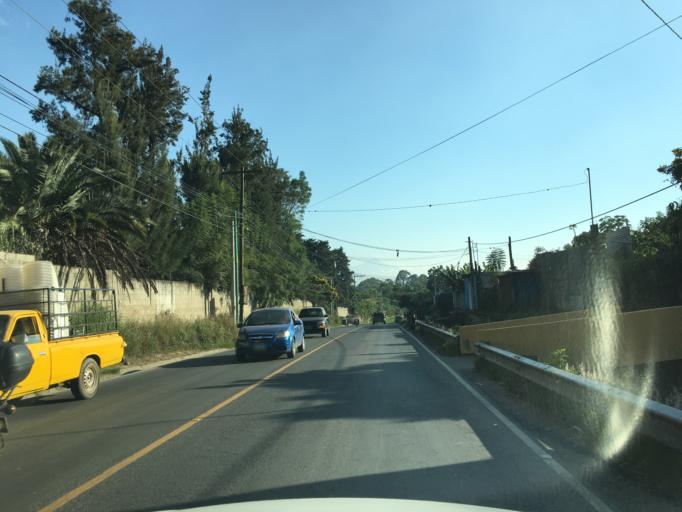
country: GT
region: Guatemala
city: Villa Nueva
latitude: 14.5386
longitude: -90.6149
